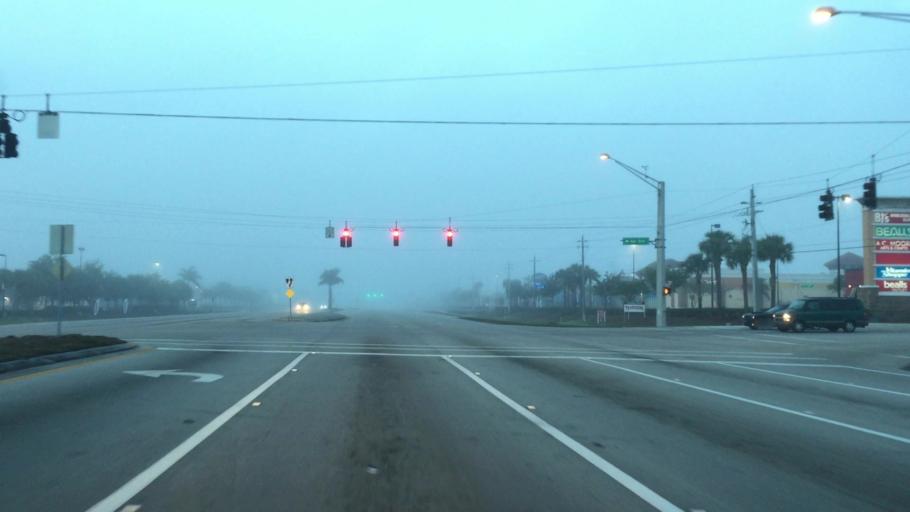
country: US
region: Florida
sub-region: Lee County
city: Fort Myers
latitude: 26.6094
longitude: -81.8113
